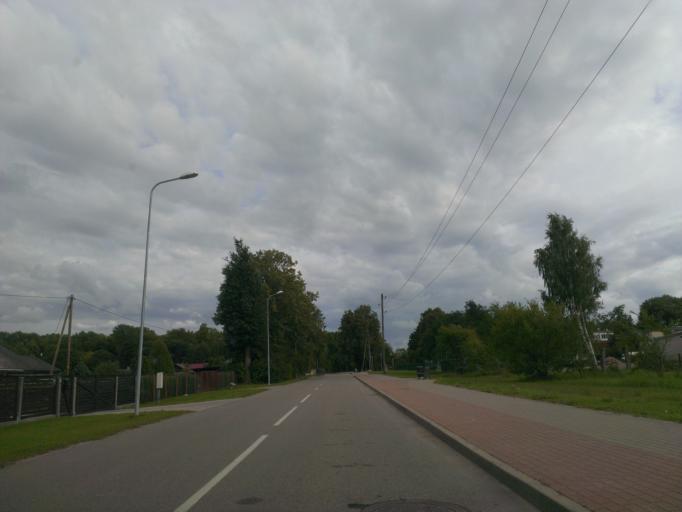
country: LV
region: Ikskile
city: Ikskile
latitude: 56.8316
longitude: 24.4851
